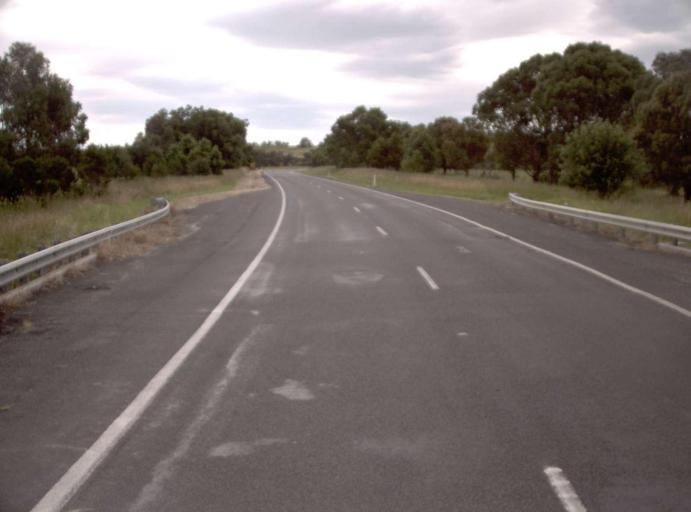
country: AU
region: Victoria
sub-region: Wellington
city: Sale
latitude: -38.2959
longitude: 147.0343
